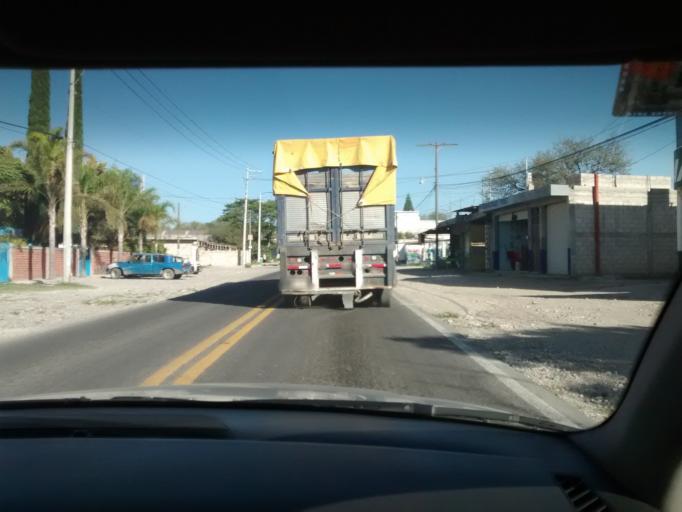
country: MX
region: Puebla
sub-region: Tepanco de Lopez
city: San Andres Cacaloapan
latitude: 18.5524
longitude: -97.5547
